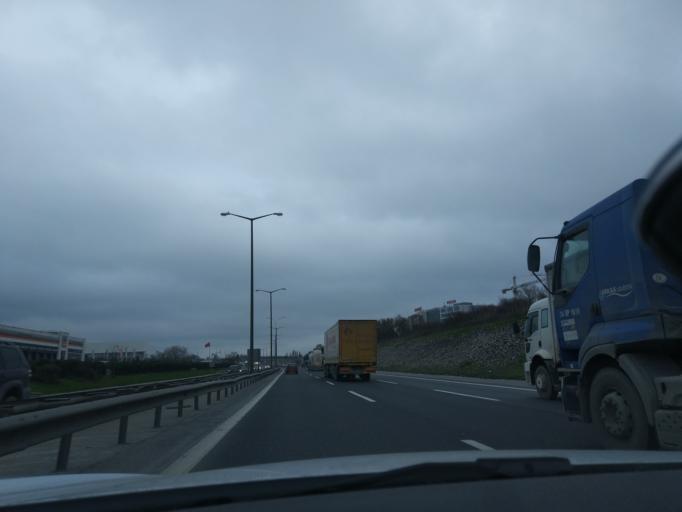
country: TR
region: Istanbul
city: Esenyurt
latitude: 41.0692
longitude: 28.6499
